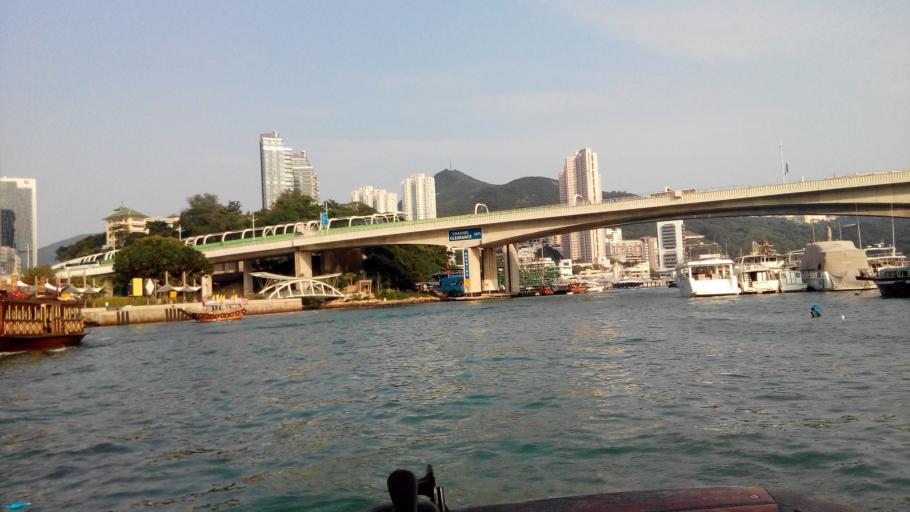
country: HK
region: Central and Western
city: Central
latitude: 22.2466
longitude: 114.1581
